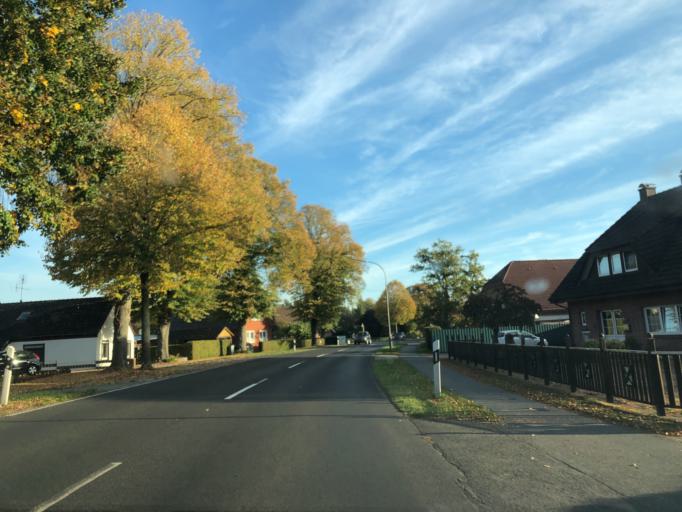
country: DE
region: Lower Saxony
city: Papenburg
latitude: 53.0703
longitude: 7.3763
